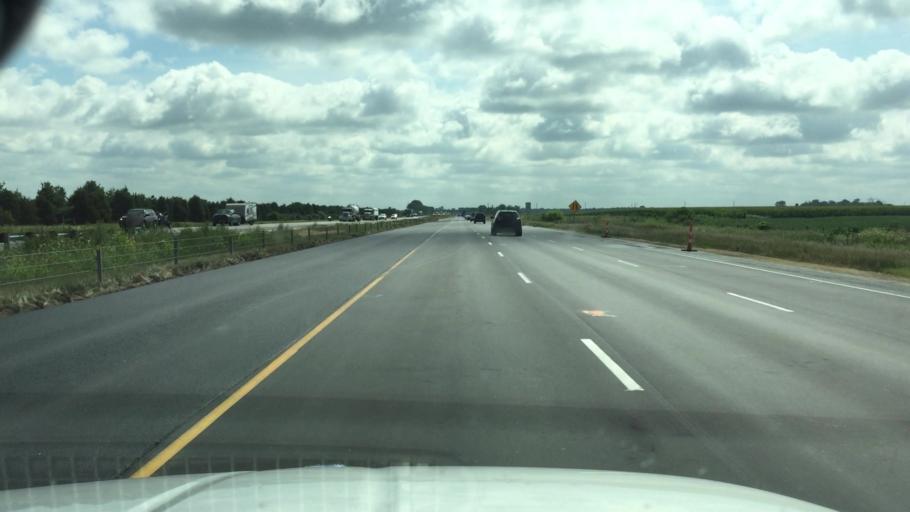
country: US
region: Iowa
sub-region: Scott County
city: Eldridge
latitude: 41.6033
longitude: -90.6630
